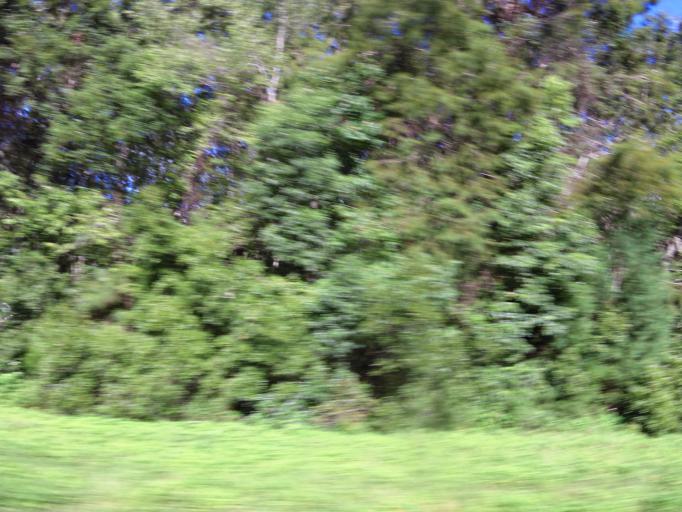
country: US
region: Georgia
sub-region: Camden County
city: Woodbine
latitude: 30.9820
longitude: -81.7277
